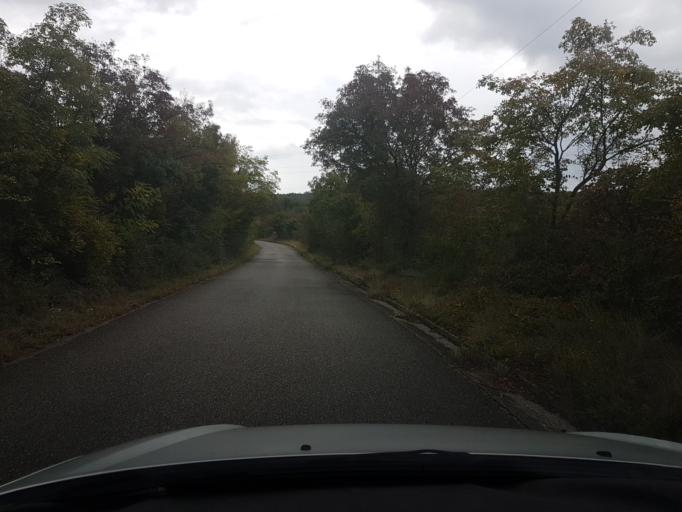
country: IT
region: Friuli Venezia Giulia
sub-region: Provincia di Gorizia
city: Doberdo del Lago
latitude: 45.8335
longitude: 13.5493
